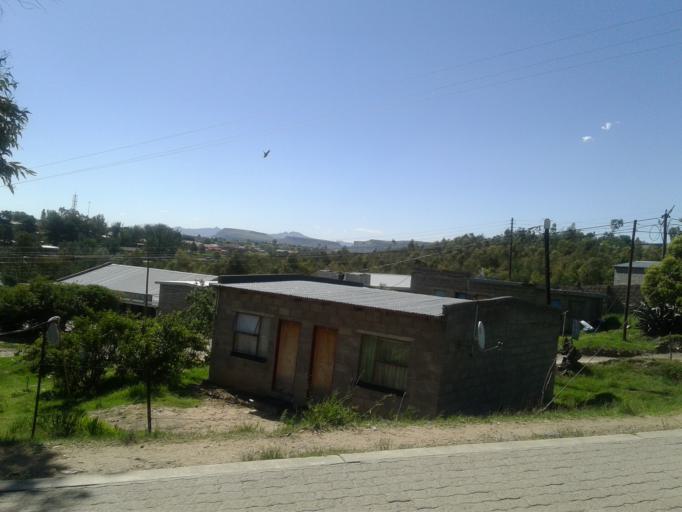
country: LS
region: Butha-Buthe
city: Butha-Buthe
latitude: -28.7647
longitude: 28.2547
